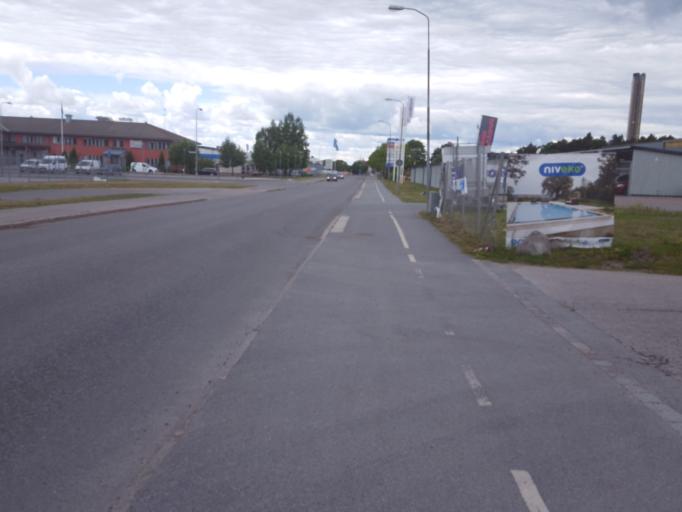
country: SE
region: Uppsala
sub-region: Uppsala Kommun
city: Saevja
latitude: 59.8481
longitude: 17.6858
